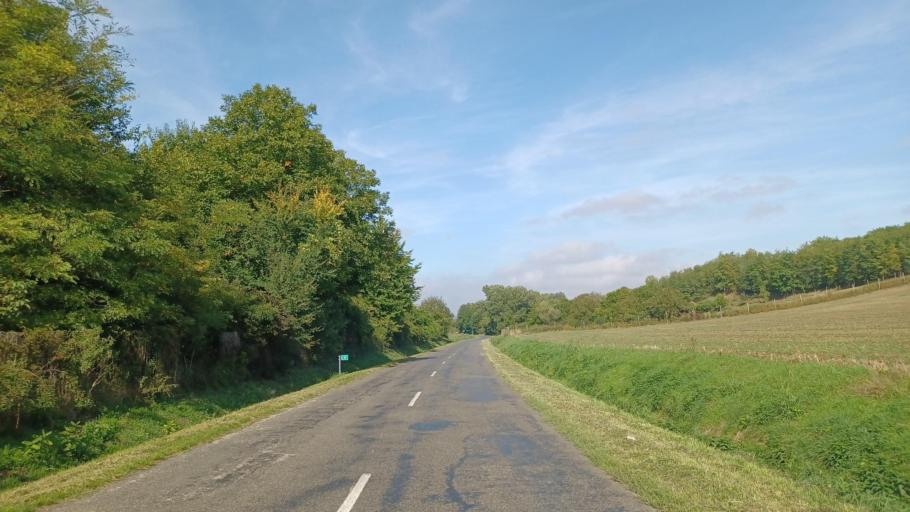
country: HU
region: Tolna
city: Pincehely
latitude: 46.6892
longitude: 18.4589
